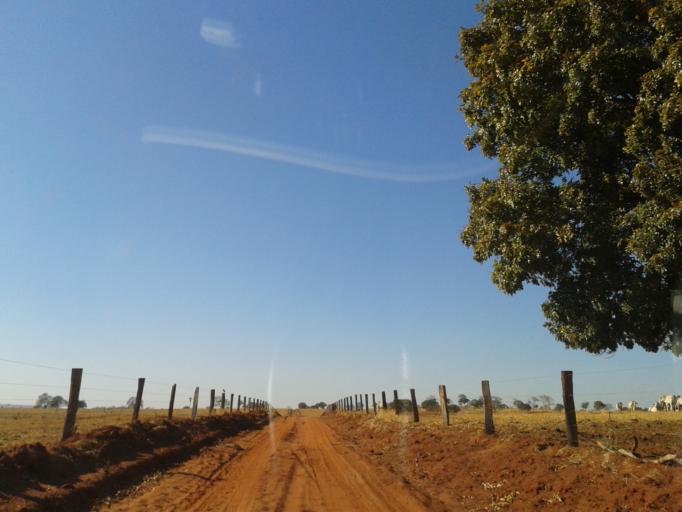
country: BR
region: Minas Gerais
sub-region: Santa Vitoria
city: Santa Vitoria
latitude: -19.0499
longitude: -49.9365
